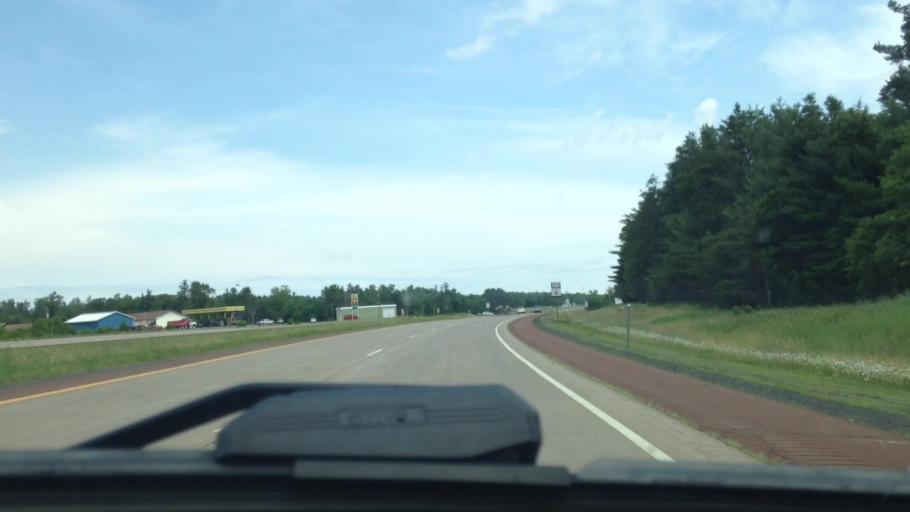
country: US
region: Wisconsin
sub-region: Douglas County
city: Lake Nebagamon
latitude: 46.3493
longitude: -91.8357
